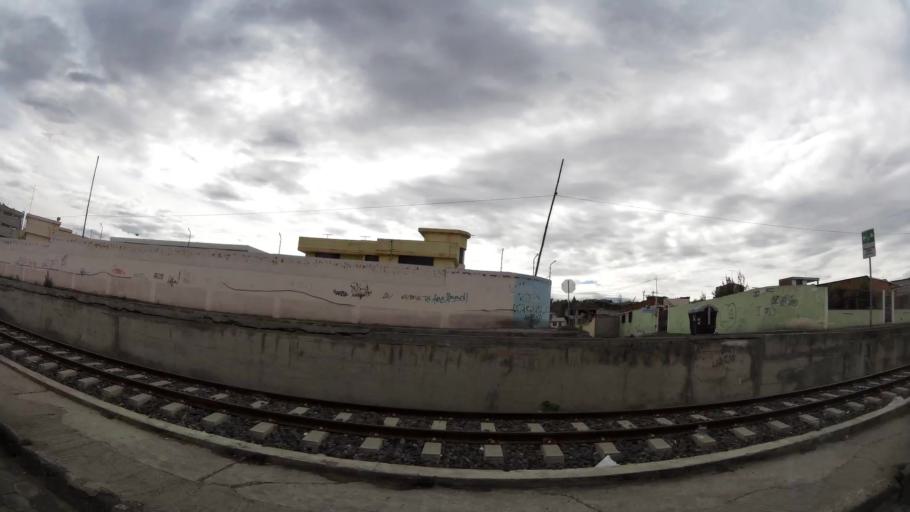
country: EC
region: Cotopaxi
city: Latacunga
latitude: -0.9406
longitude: -78.6183
